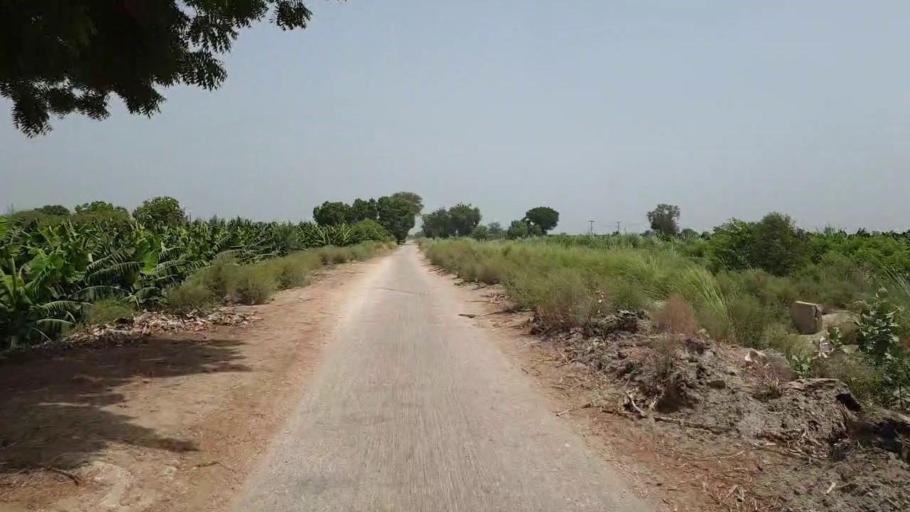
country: PK
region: Sindh
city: Nawabshah
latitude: 26.2807
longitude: 68.3120
